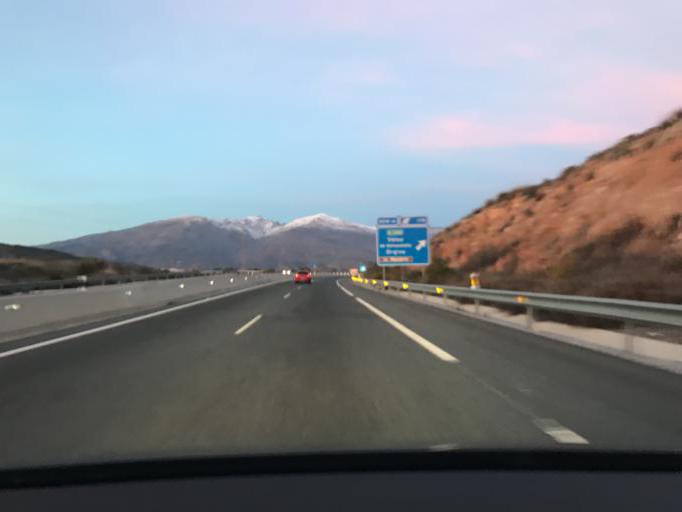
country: ES
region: Andalusia
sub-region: Provincia de Granada
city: Velez de Benaudalla
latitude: 36.8417
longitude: -3.4996
